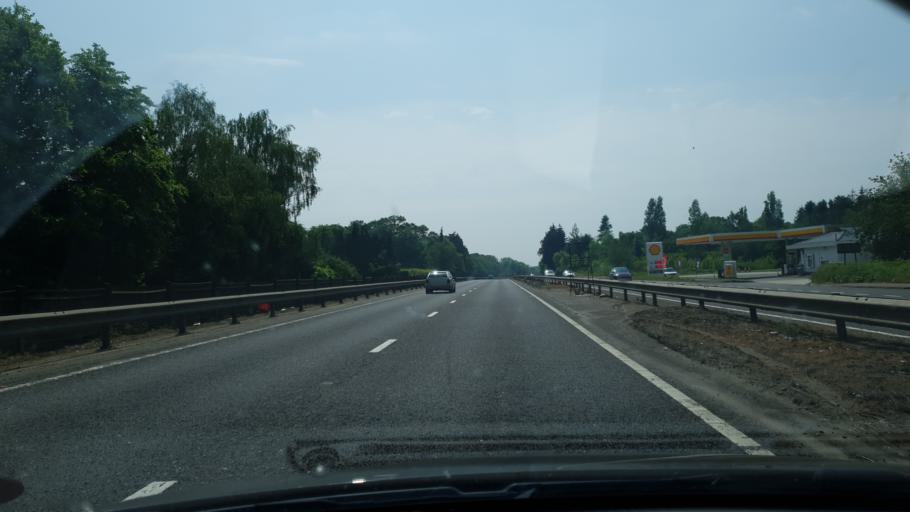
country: GB
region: England
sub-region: Essex
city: Colchester
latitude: 51.9390
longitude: 0.9523
